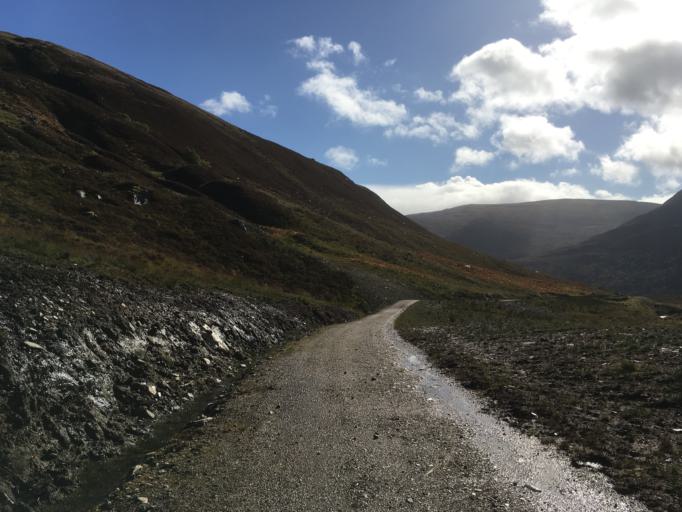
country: GB
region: Scotland
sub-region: Highland
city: Spean Bridge
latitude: 57.3504
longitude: -4.9838
